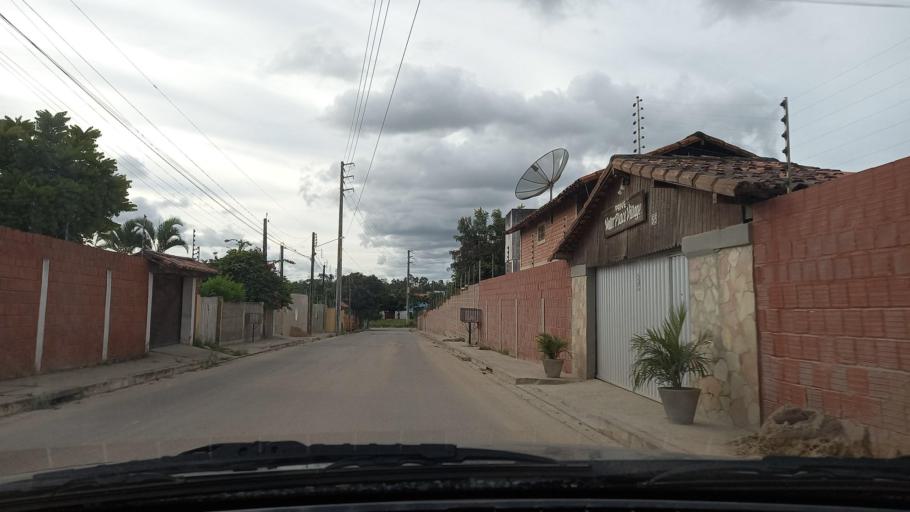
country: BR
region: Pernambuco
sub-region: Gravata
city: Gravata
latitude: -8.1978
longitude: -35.5411
